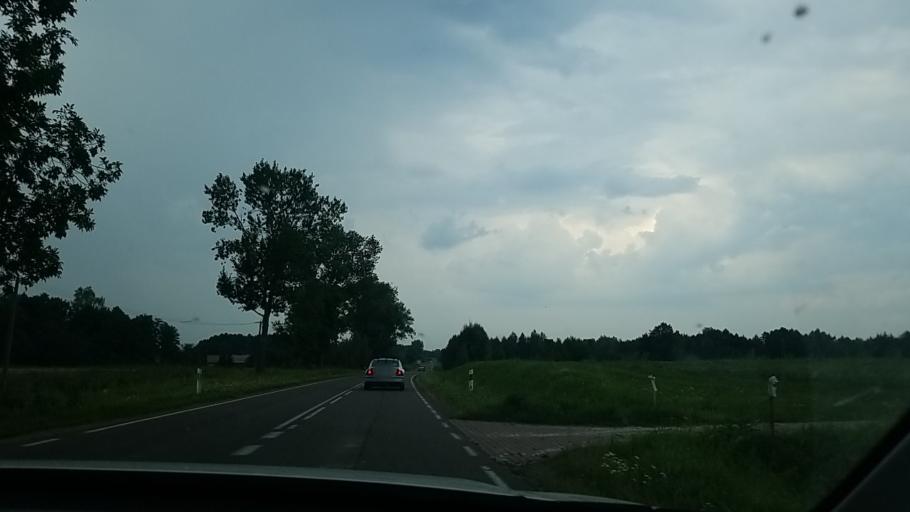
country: PL
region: Lublin Voivodeship
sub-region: Powiat leczynski
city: Cycow
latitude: 51.2768
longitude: 23.0977
